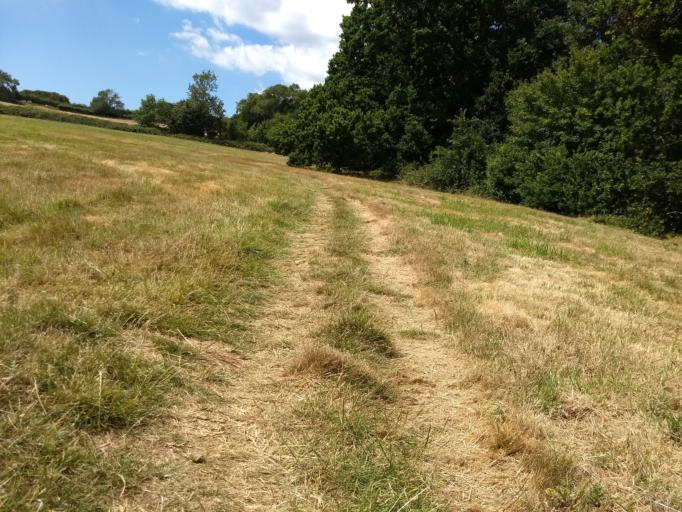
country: GB
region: England
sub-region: Isle of Wight
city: Seaview
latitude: 50.7022
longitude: -1.1034
